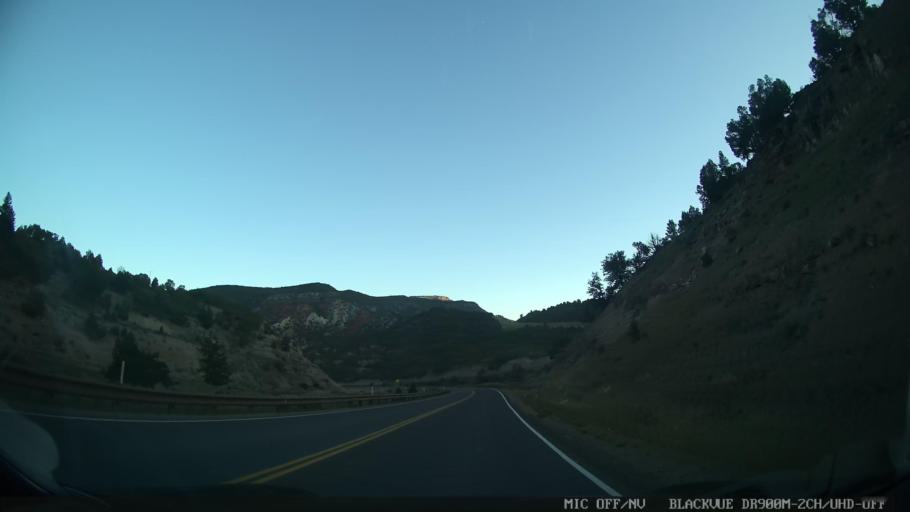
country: US
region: Colorado
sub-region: Eagle County
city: Edwards
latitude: 39.8536
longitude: -106.6459
